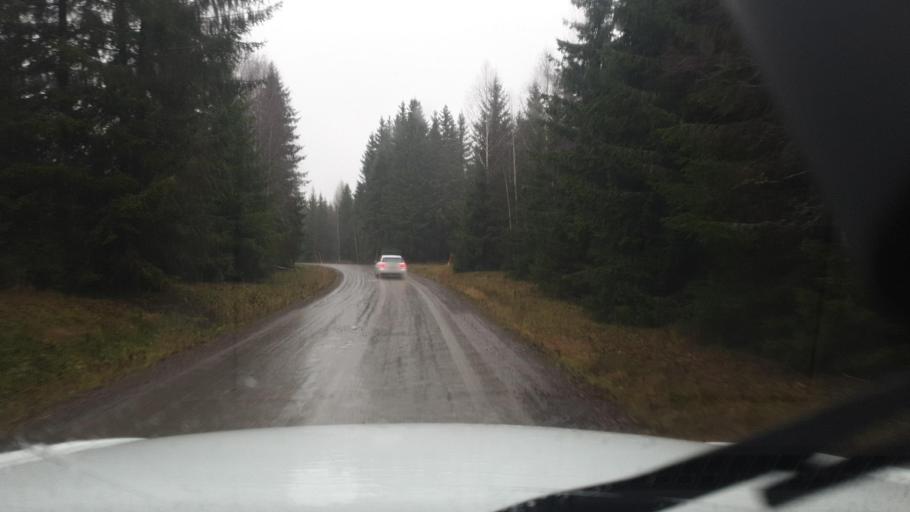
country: SE
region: Vaermland
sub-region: Sunne Kommun
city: Sunne
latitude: 59.8091
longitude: 13.0693
